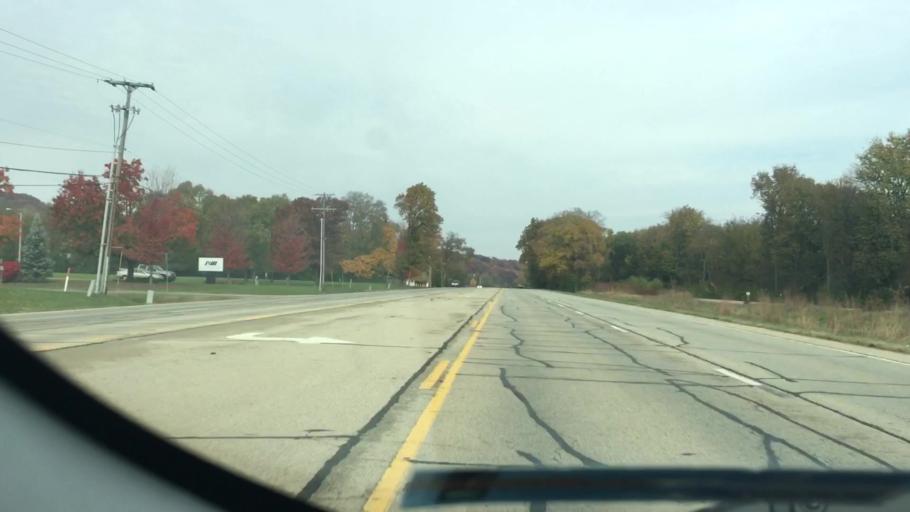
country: US
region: Illinois
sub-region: Peoria County
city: Peoria Heights
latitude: 40.7664
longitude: -89.5699
